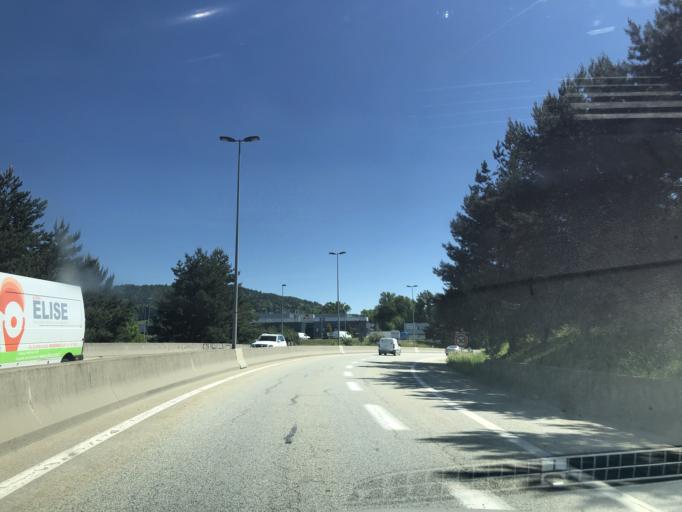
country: FR
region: Rhone-Alpes
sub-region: Departement de la Haute-Savoie
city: Pringy
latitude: 45.9362
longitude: 6.1271
